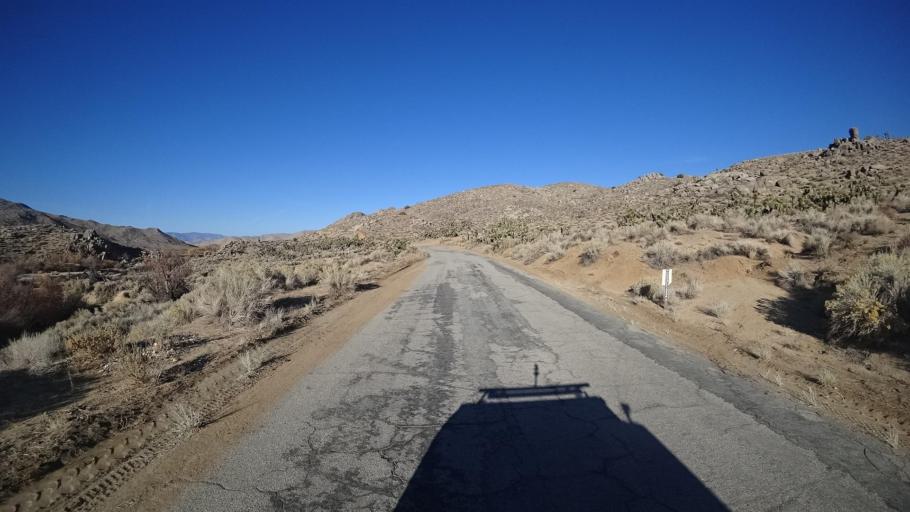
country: US
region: California
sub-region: Kern County
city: Weldon
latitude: 35.4879
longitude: -118.2048
